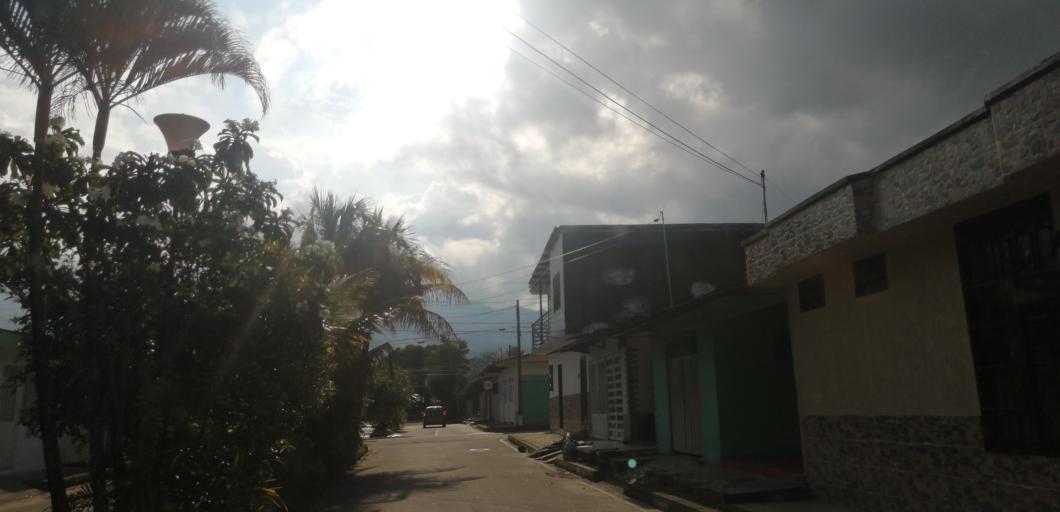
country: CO
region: Meta
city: Acacias
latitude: 3.9865
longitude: -73.7764
